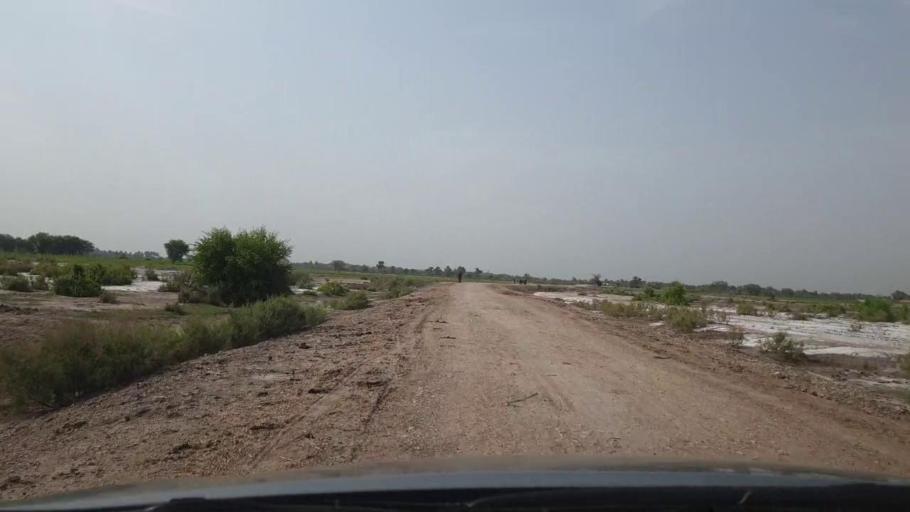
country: PK
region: Sindh
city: Rohri
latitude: 27.6698
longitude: 69.0135
